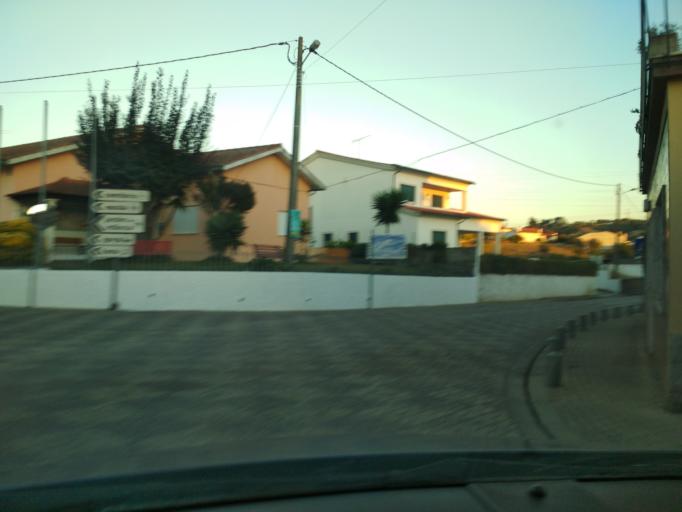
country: PT
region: Coimbra
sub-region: Coimbra
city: Coimbra
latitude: 40.1675
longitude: -8.4637
